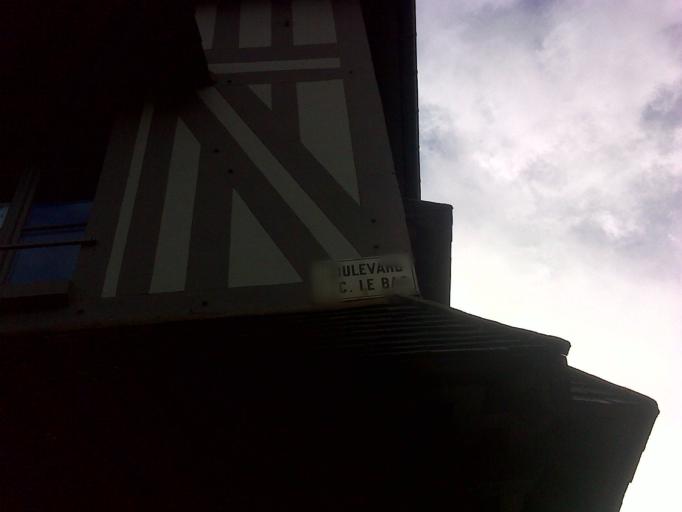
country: FR
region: Haute-Normandie
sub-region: Departement de la Seine-Maritime
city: La Feuillie
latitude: 49.3986
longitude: 1.4768
